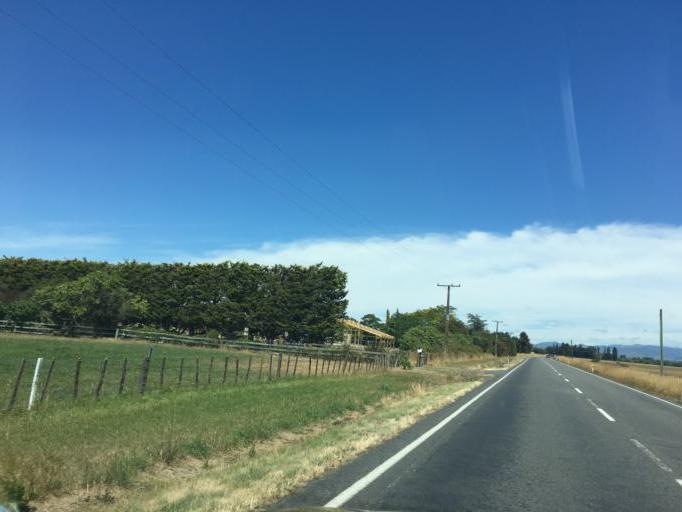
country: NZ
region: Hawke's Bay
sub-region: Hastings District
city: Hastings
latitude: -39.9974
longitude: 176.4147
